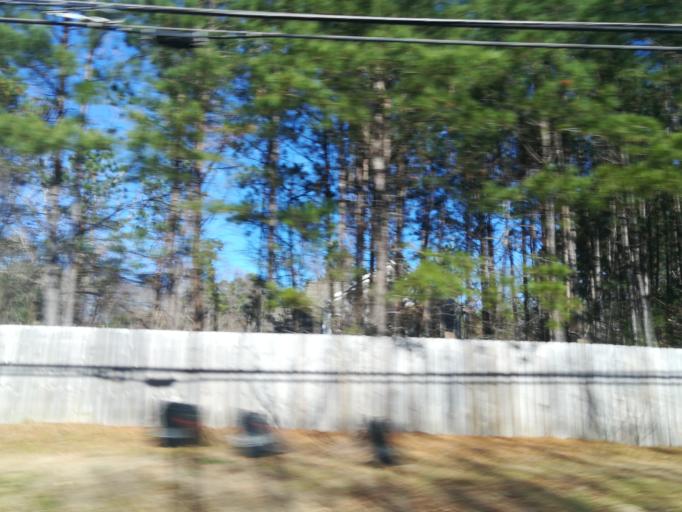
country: US
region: North Carolina
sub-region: Durham County
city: Durham
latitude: 36.0325
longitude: -78.9849
